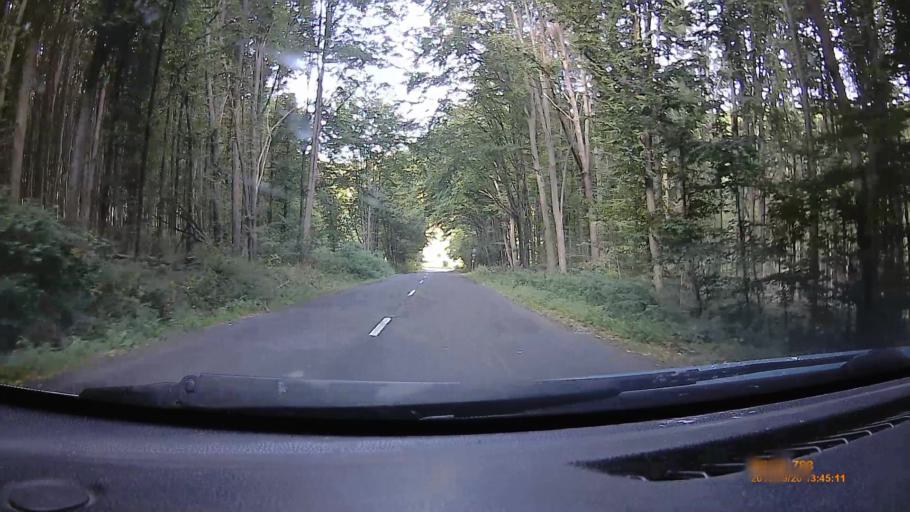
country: HU
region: Borsod-Abauj-Zemplen
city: Saly
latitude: 48.0633
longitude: 20.5637
